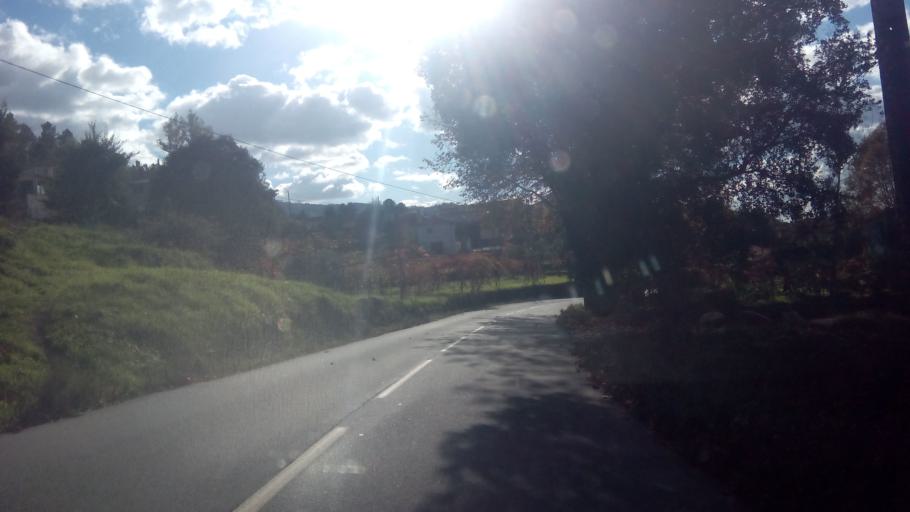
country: PT
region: Porto
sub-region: Amarante
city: Amarante
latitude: 41.2613
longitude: -8.0232
